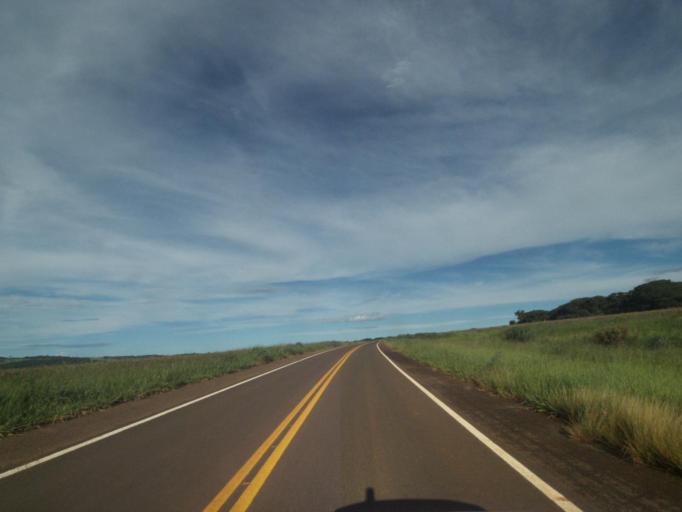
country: BR
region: Goias
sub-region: Jaragua
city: Jaragua
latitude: -15.9022
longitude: -49.5377
